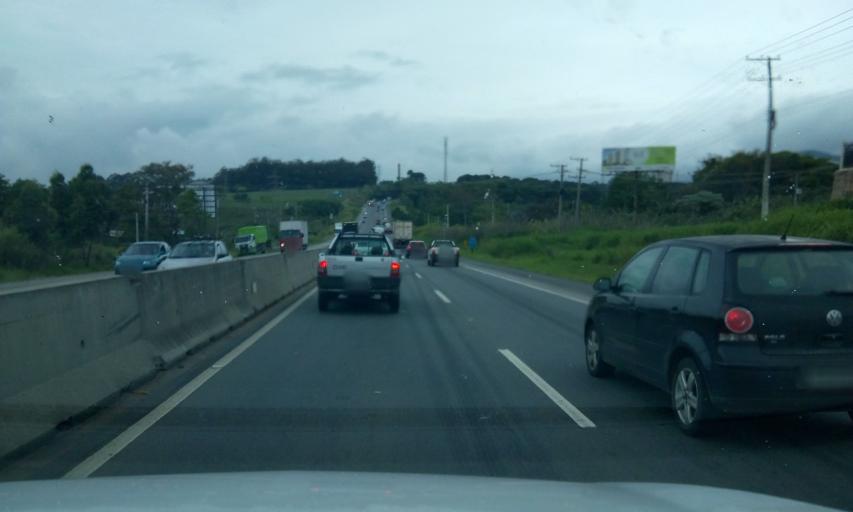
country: BR
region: Sao Paulo
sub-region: Itupeva
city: Itupeva
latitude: -23.1777
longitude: -46.9788
